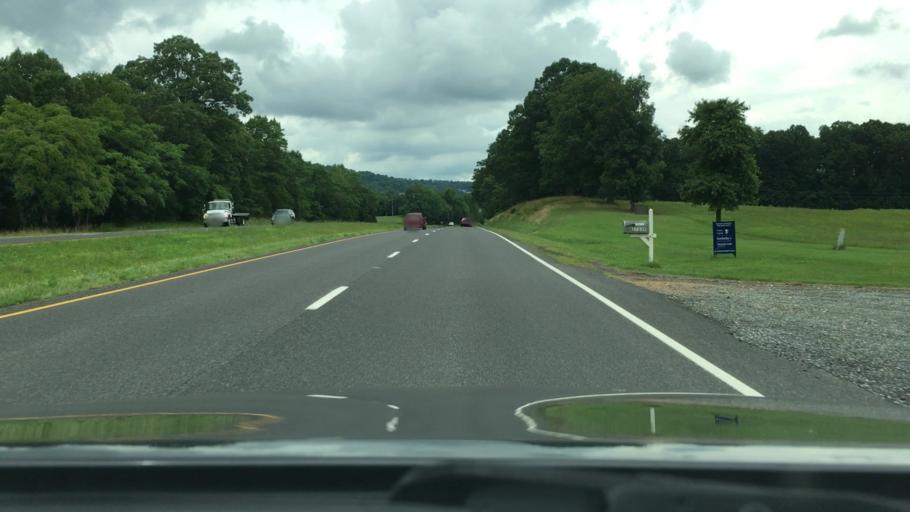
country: US
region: Virginia
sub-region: Orange County
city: Gordonsville
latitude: 38.1664
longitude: -78.1600
